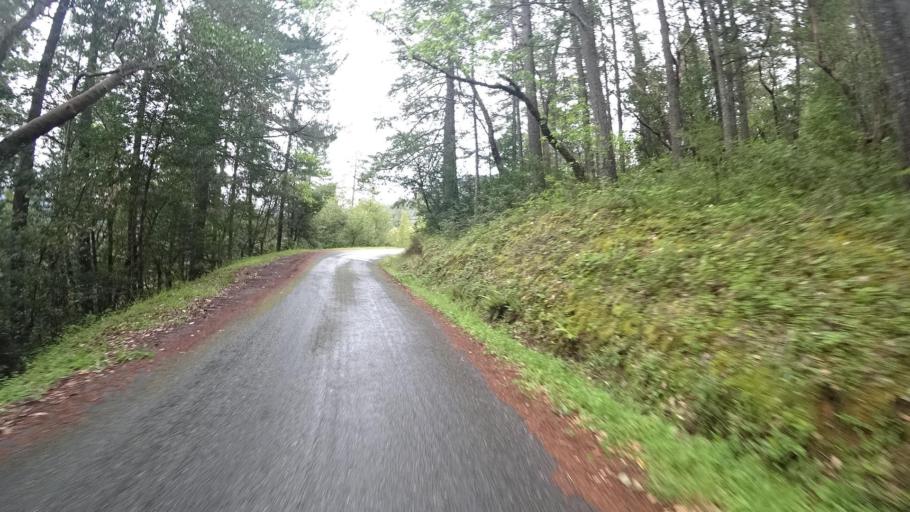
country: US
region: California
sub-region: Humboldt County
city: Willow Creek
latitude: 41.3647
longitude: -123.5056
